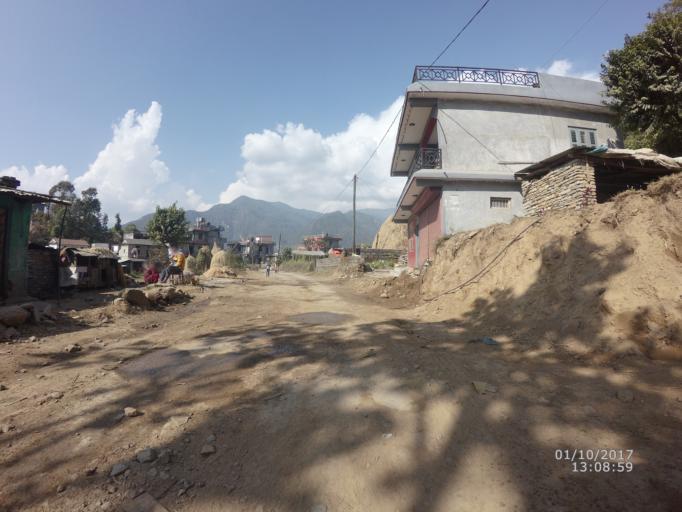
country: NP
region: Western Region
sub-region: Gandaki Zone
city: Pokhara
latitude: 28.3090
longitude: 83.9594
